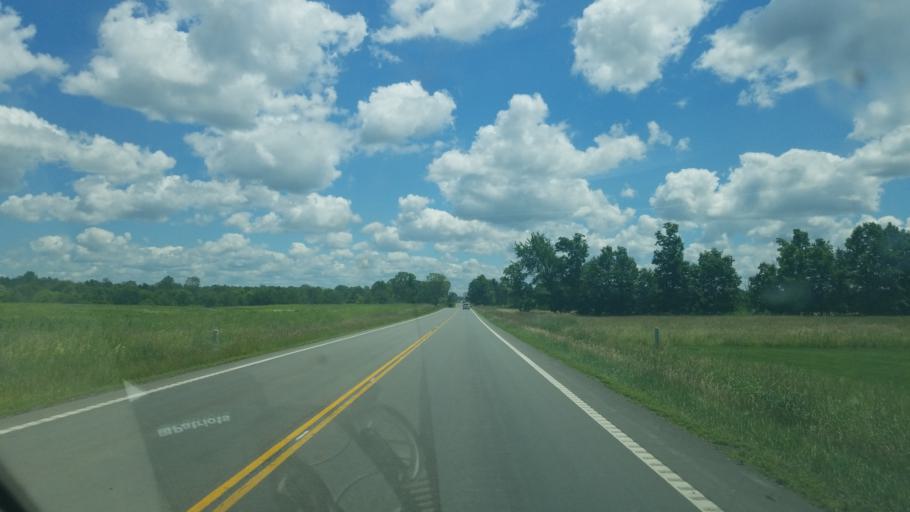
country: US
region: Ohio
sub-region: Huron County
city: New London
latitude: 41.0296
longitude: -82.3728
